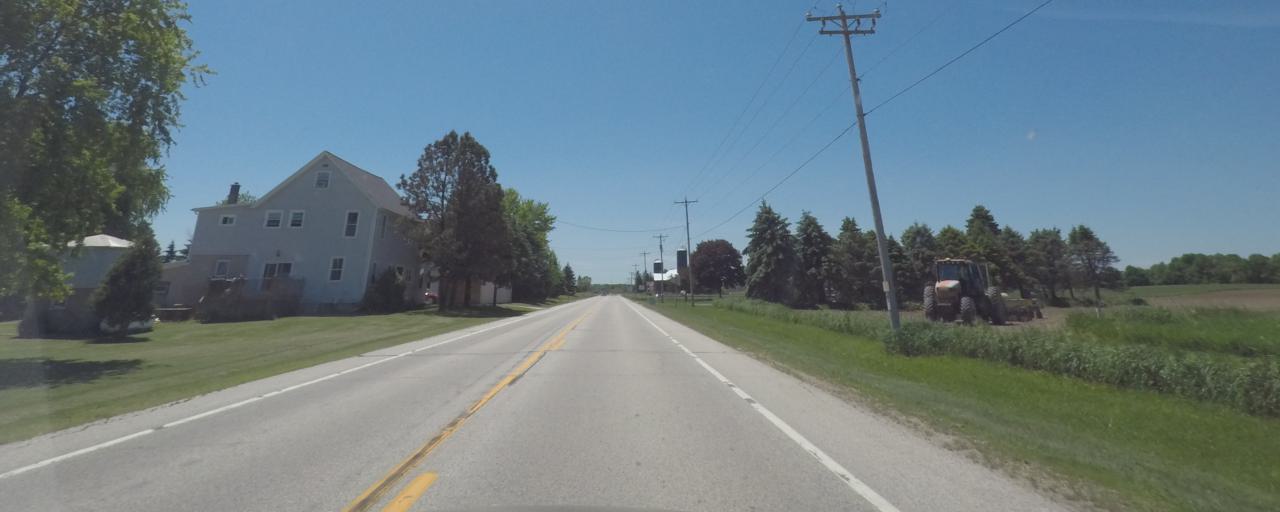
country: US
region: Wisconsin
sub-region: Ozaukee County
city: Kohler
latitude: 43.5615
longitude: -88.0709
